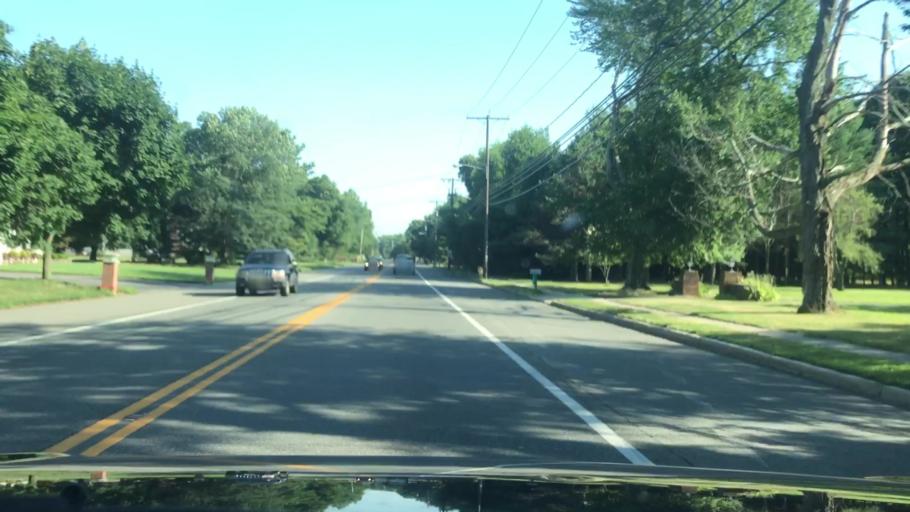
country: US
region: New Jersey
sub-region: Ocean County
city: Leisure Village
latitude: 40.0257
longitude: -74.2009
